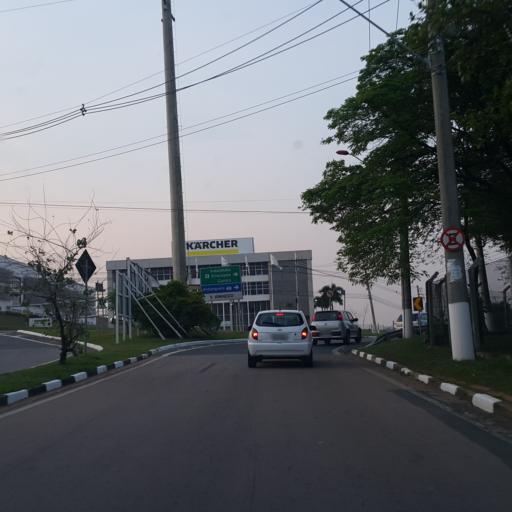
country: BR
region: Sao Paulo
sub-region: Vinhedo
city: Vinhedo
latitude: -23.0624
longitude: -46.9992
